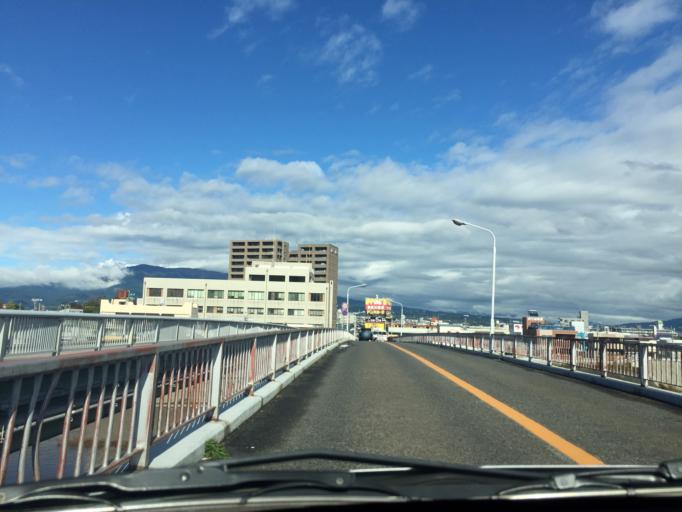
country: JP
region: Shizuoka
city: Numazu
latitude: 35.0982
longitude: 138.8706
